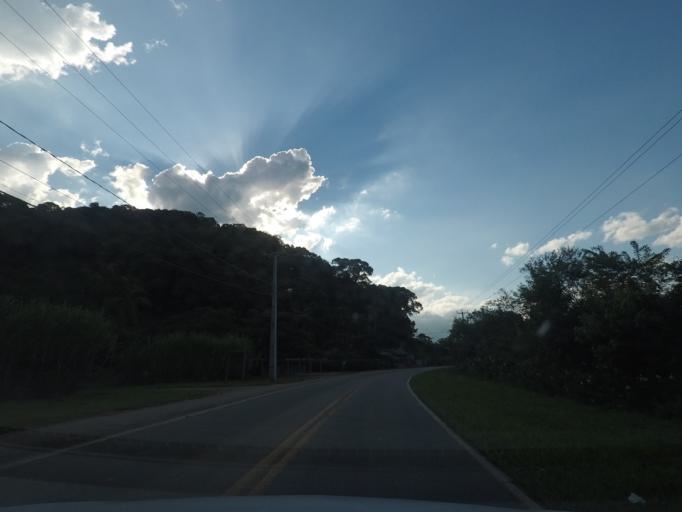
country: BR
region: Parana
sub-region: Antonina
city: Antonina
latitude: -25.4438
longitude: -48.8752
